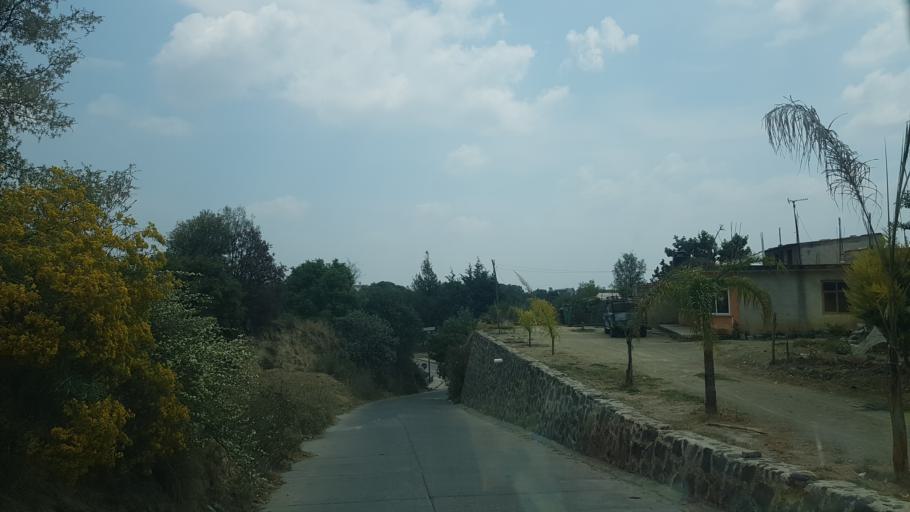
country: MX
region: Puebla
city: Domingo Arenas
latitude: 19.1386
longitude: -98.4776
